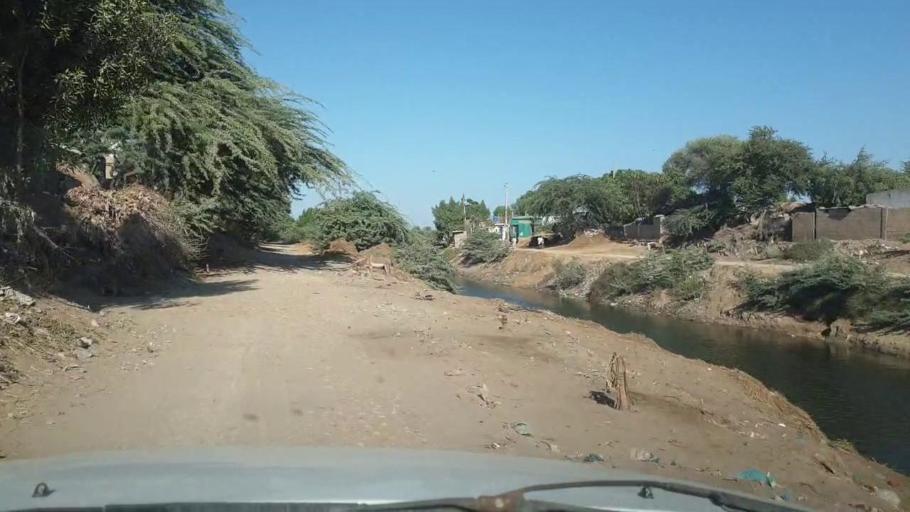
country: PK
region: Sindh
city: Thatta
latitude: 24.5538
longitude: 67.8430
